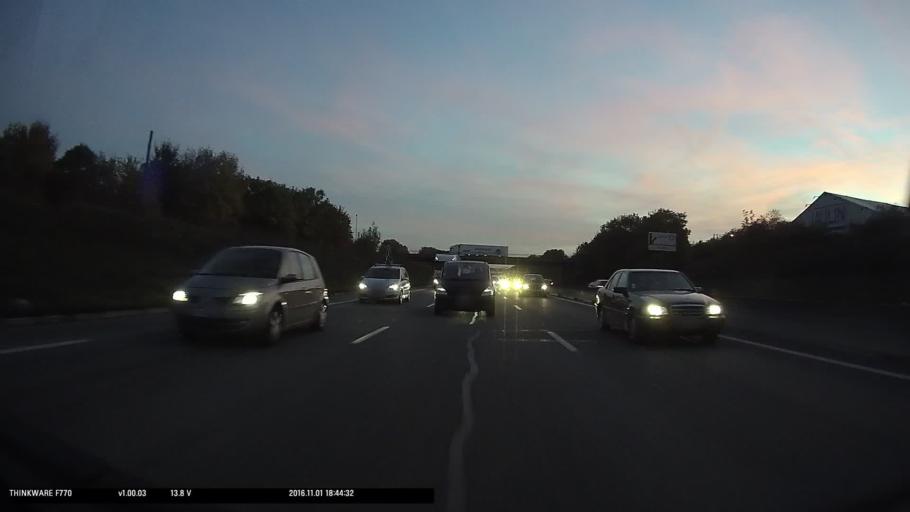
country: FR
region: Ile-de-France
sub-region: Departement de l'Essonne
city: Chilly-Mazarin
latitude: 48.7134
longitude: 2.3085
